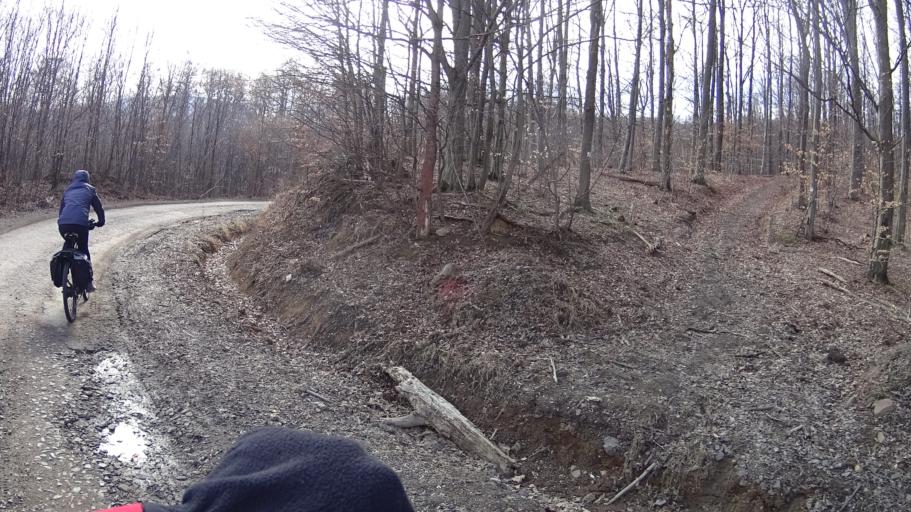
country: HU
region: Heves
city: Paradsasvar
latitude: 47.9179
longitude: 19.9732
